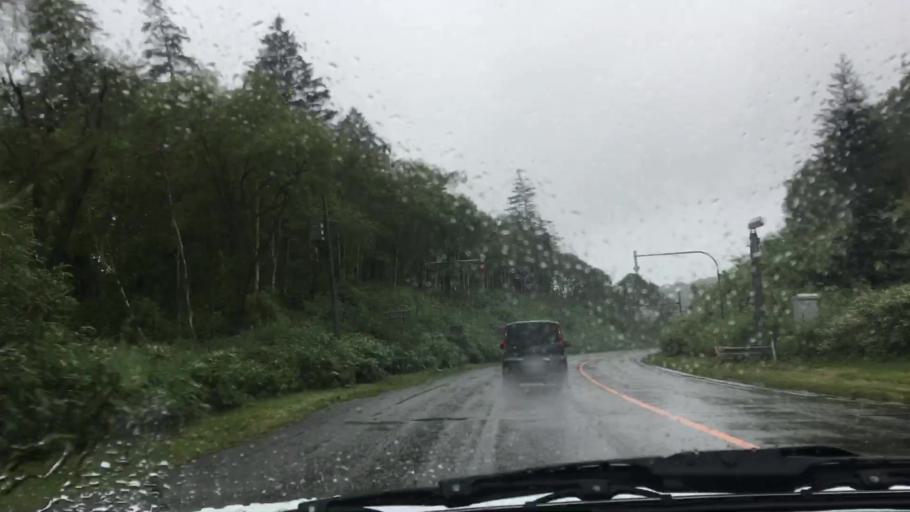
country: JP
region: Hokkaido
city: Sapporo
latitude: 42.8656
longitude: 141.1096
